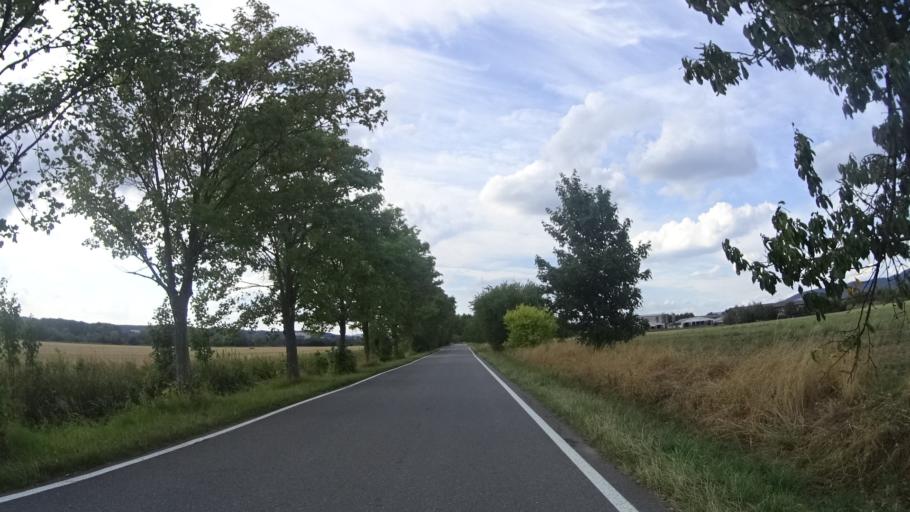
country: CZ
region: Olomoucky
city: Dubicko
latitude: 49.8192
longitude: 16.9394
